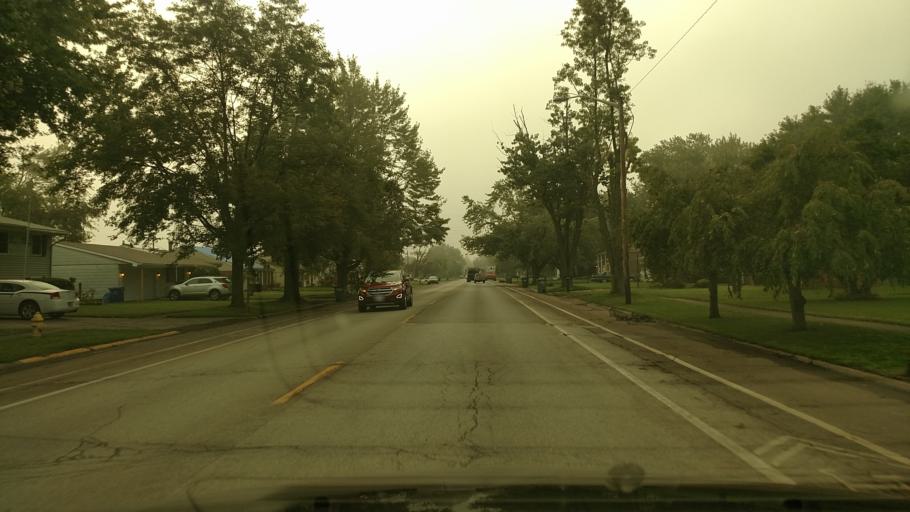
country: US
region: Indiana
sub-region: Howard County
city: Kokomo
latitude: 40.4618
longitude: -86.1519
